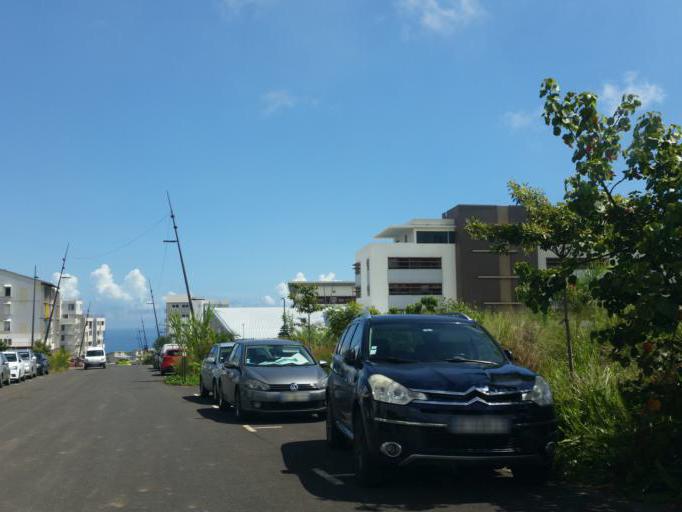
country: RE
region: Reunion
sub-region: Reunion
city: Sainte-Marie
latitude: -20.9224
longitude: 55.5293
